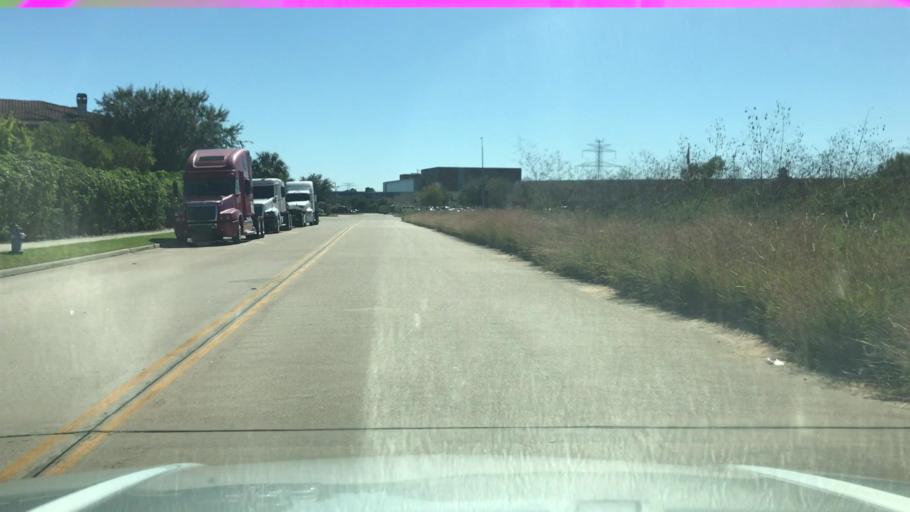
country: US
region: Texas
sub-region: Fort Bend County
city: Cinco Ranch
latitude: 29.7796
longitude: -95.7458
